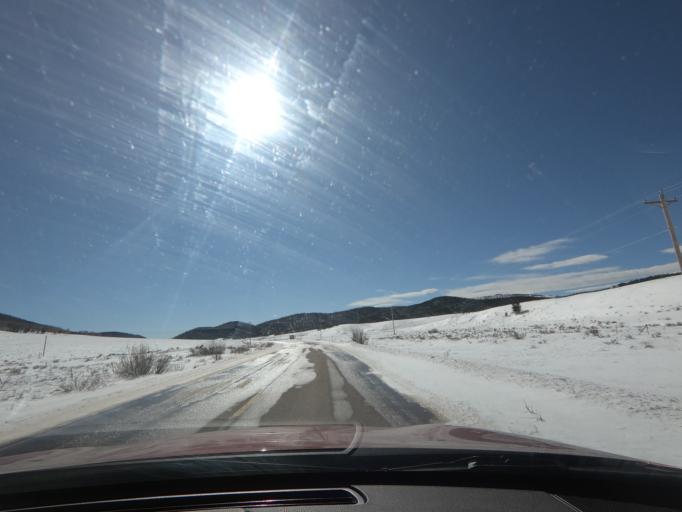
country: US
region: Colorado
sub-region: Teller County
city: Cripple Creek
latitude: 38.7749
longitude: -105.1217
